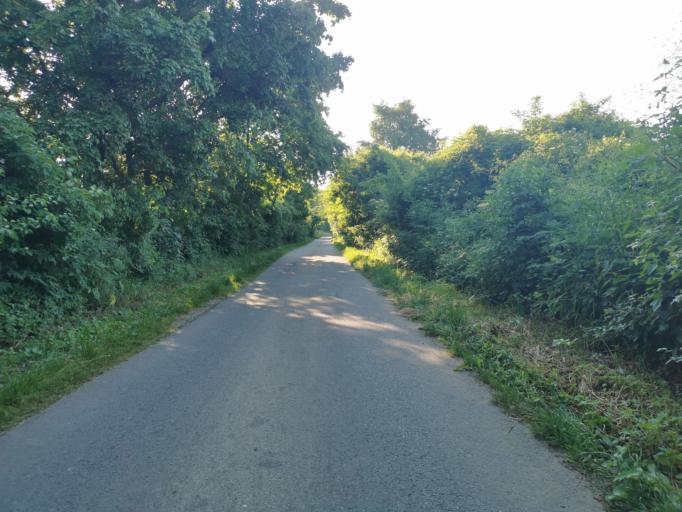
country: CZ
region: South Moravian
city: Straznice
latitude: 48.8830
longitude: 17.3457
